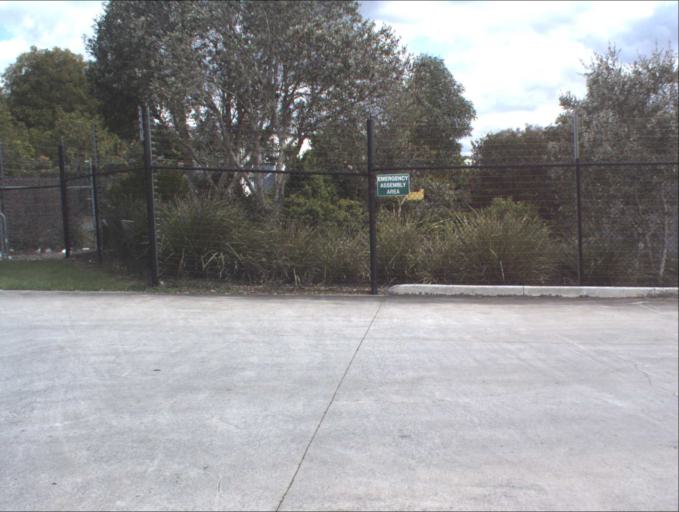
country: AU
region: Queensland
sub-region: Logan
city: Logan Reserve
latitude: -27.6808
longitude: 153.0735
